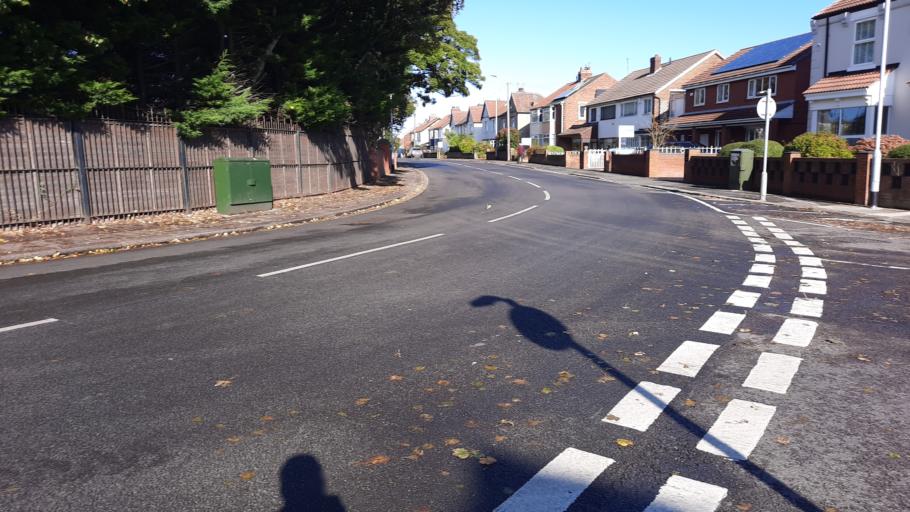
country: GB
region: England
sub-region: Hartlepool
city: Hartlepool
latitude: 54.6716
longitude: -1.2157
